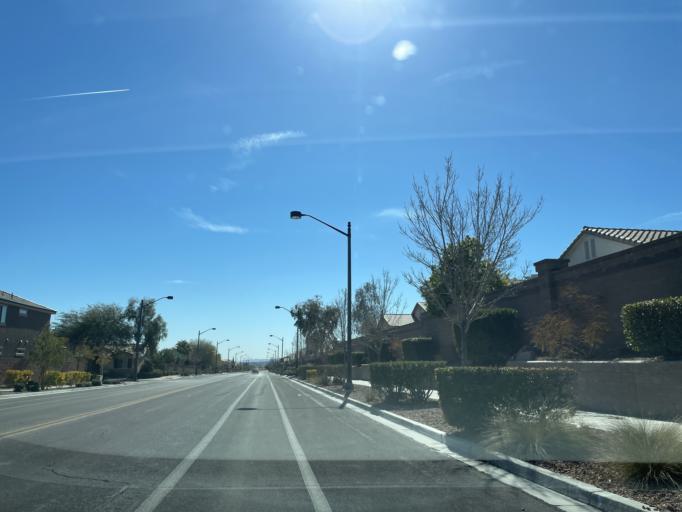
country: US
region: Nevada
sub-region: Clark County
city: Summerlin South
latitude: 36.2890
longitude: -115.3015
